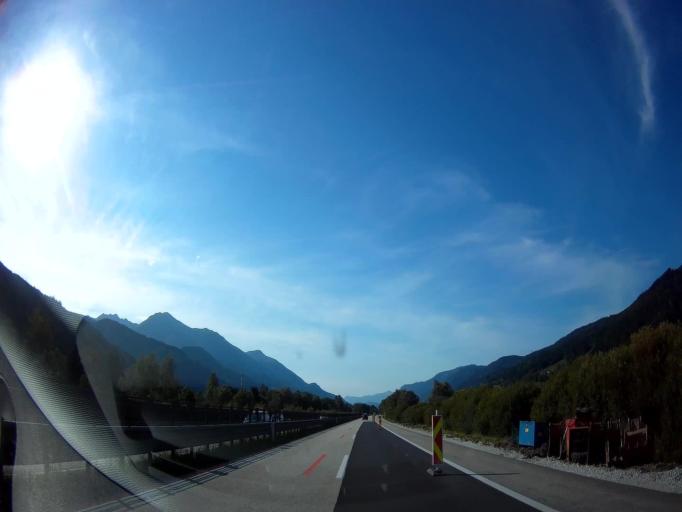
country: AT
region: Styria
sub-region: Politischer Bezirk Liezen
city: Trieben
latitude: 47.4876
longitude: 14.5205
